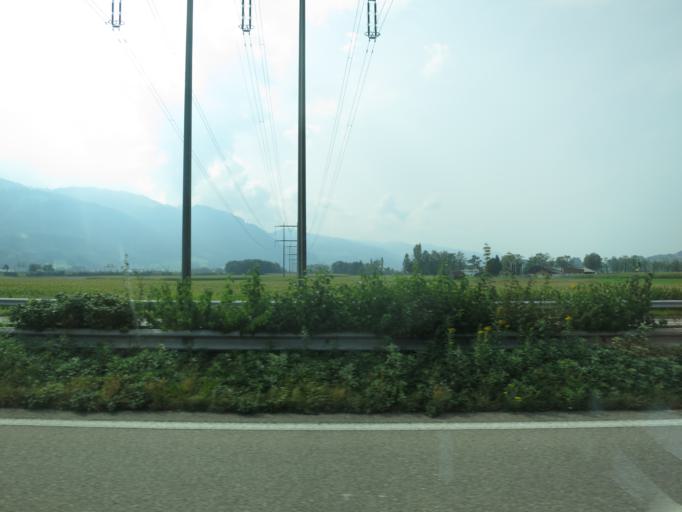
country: CH
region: Schwyz
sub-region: Bezirk March
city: Reichenburg
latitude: 47.1879
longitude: 8.9764
